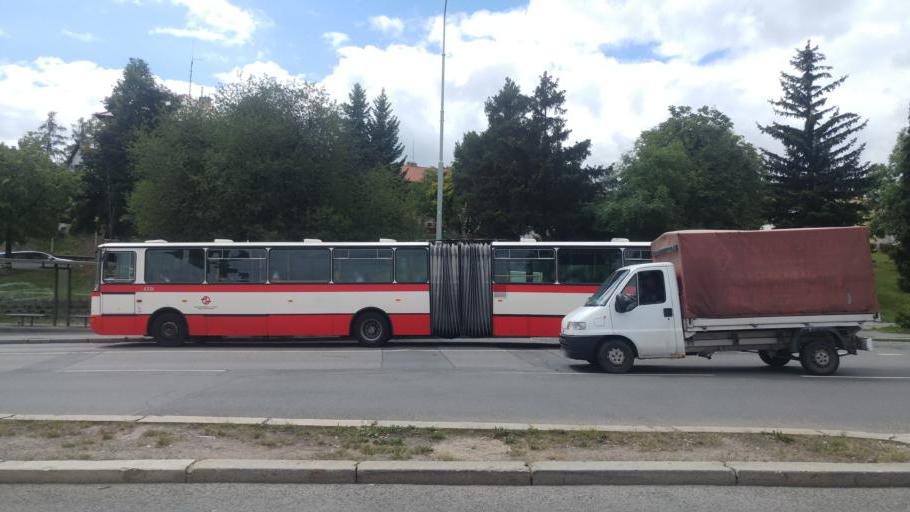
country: CZ
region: Praha
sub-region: Praha 8
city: Karlin
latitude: 50.0608
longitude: 14.4697
